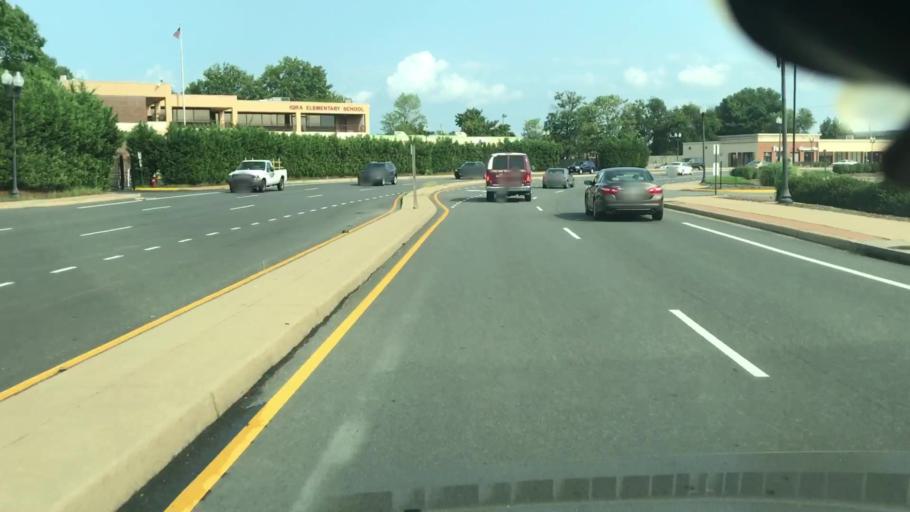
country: US
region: Virginia
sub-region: Fairfax County
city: Springfield
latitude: 38.7802
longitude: -77.1770
